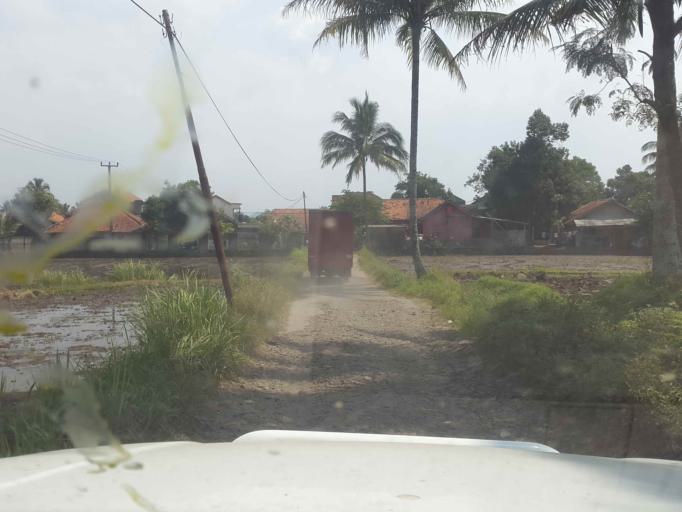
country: ID
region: West Java
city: Ciranjang-hilir
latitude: -6.8817
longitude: 107.2213
